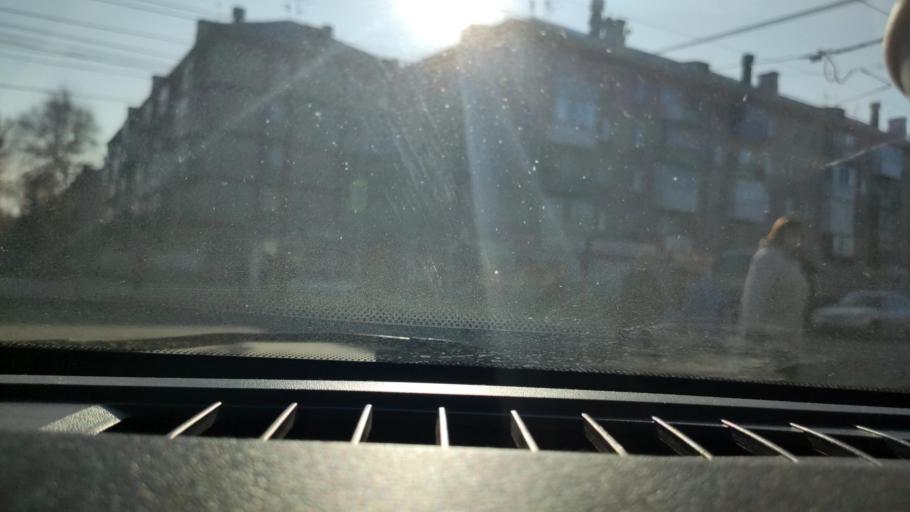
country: RU
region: Samara
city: Samara
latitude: 53.2223
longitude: 50.2691
